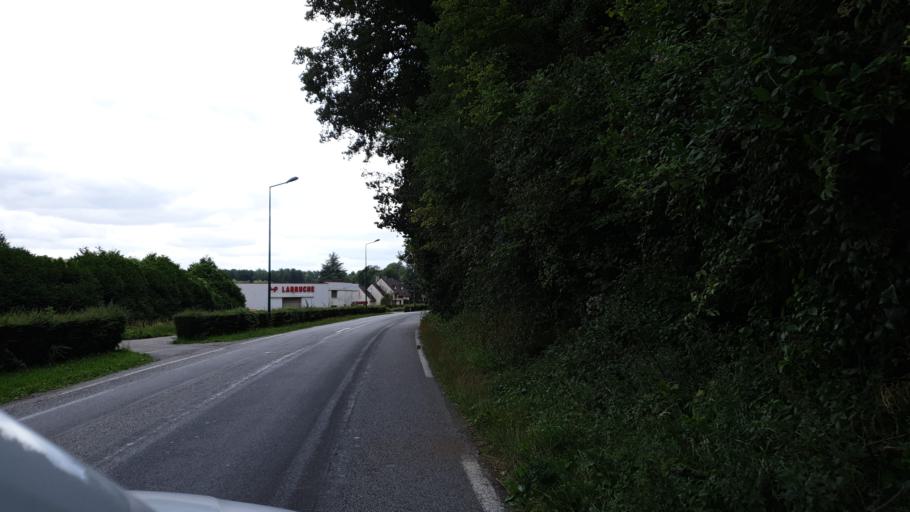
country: FR
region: Haute-Normandie
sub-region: Departement de la Seine-Maritime
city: Lillebonne
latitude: 49.5136
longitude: 0.5324
